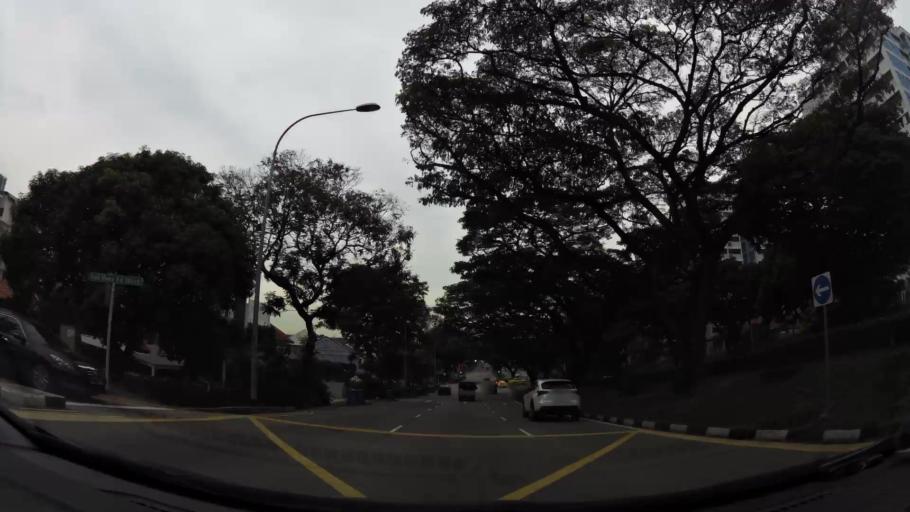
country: SG
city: Singapore
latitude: 1.3677
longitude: 103.8759
